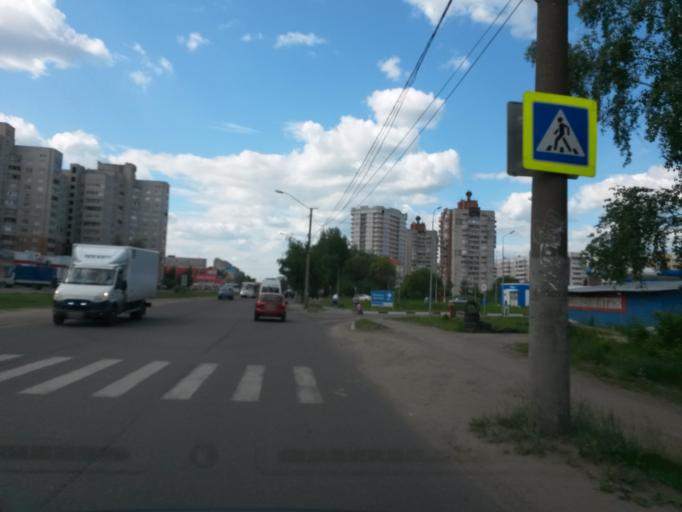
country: RU
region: Jaroslavl
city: Yaroslavl
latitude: 57.6428
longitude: 39.9585
